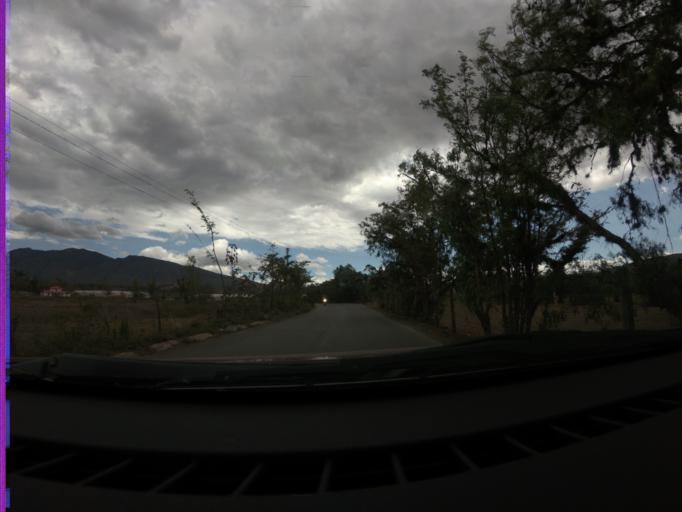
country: CO
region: Boyaca
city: Villa de Leiva
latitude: 5.6386
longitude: -73.5621
